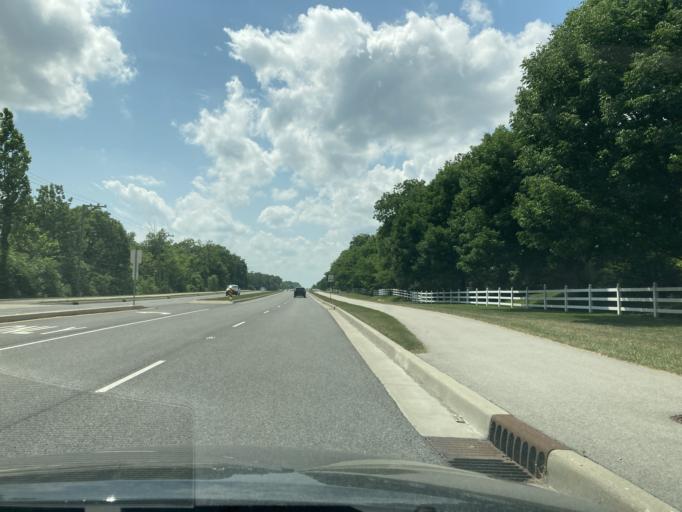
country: US
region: Indiana
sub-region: Hamilton County
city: Carmel
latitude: 39.9995
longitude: -86.1683
